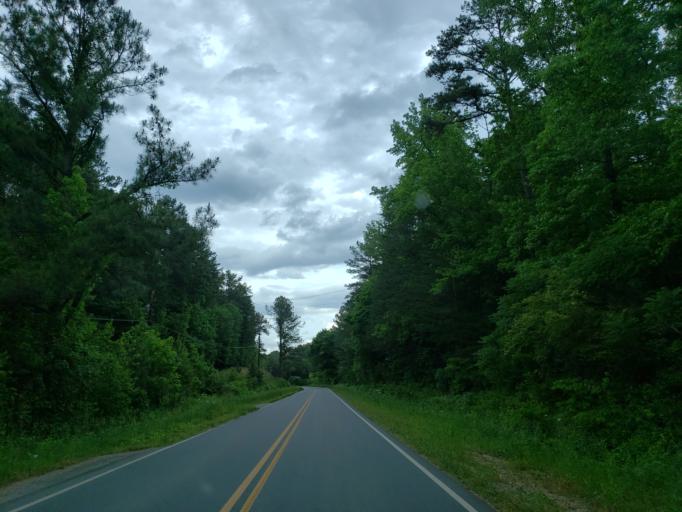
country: US
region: Georgia
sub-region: Polk County
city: Rockmart
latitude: 33.9672
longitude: -85.0480
